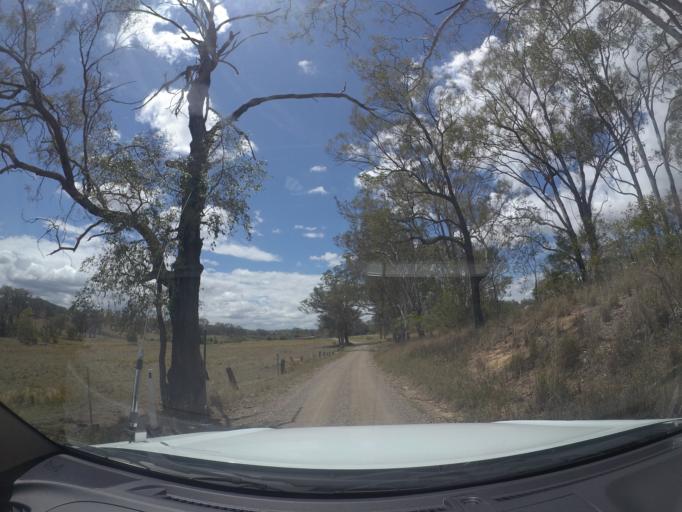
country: AU
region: Queensland
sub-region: Logan
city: Cedar Vale
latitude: -27.9024
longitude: 153.0604
